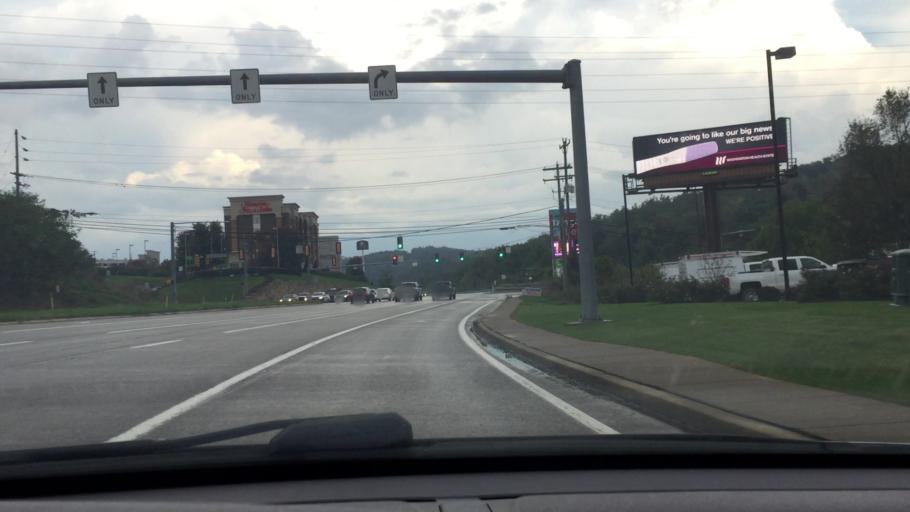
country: US
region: Pennsylvania
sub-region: Washington County
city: McGovern
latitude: 40.2218
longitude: -80.2079
